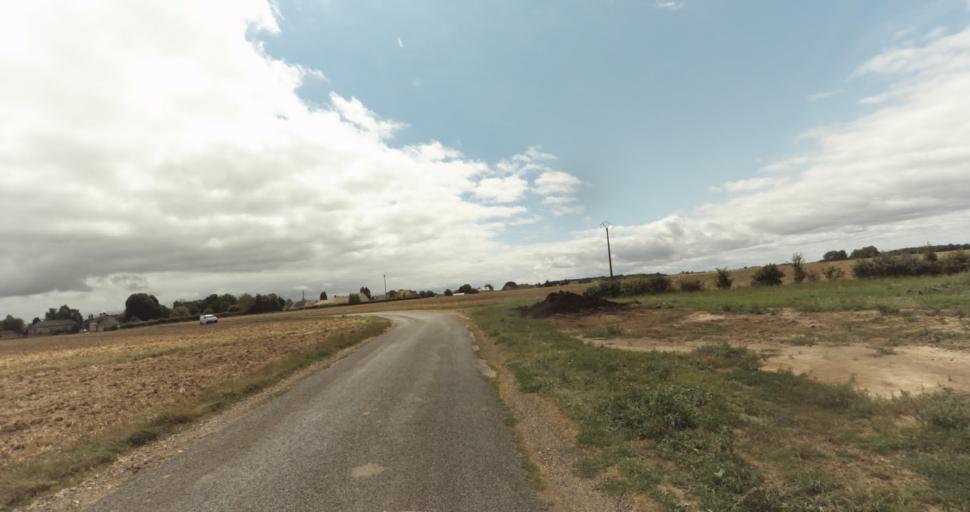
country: FR
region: Haute-Normandie
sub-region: Departement de l'Eure
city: La Madeleine-de-Nonancourt
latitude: 48.9045
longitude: 1.2360
